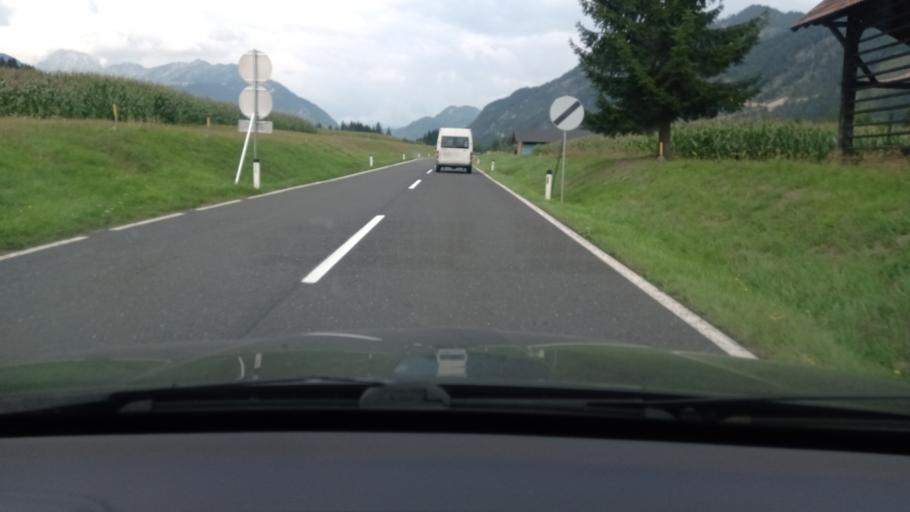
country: AT
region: Carinthia
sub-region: Politischer Bezirk Hermagor
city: Hermagor
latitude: 46.6626
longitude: 13.3094
